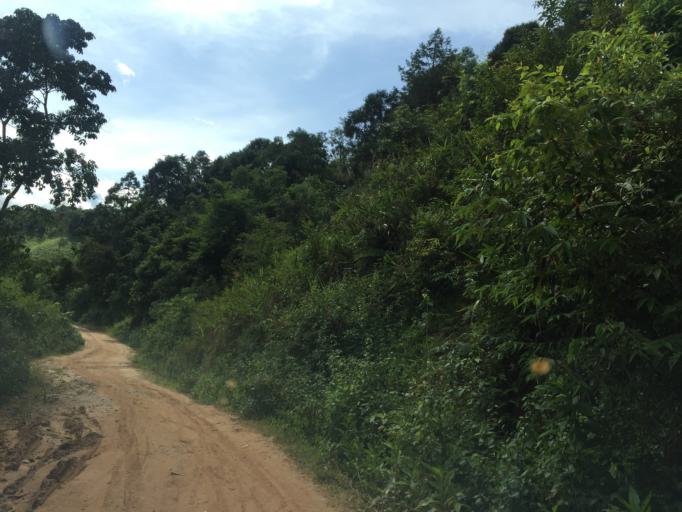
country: LA
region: Xiangkhoang
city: Muang Phonsavan
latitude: 19.3291
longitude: 103.4696
